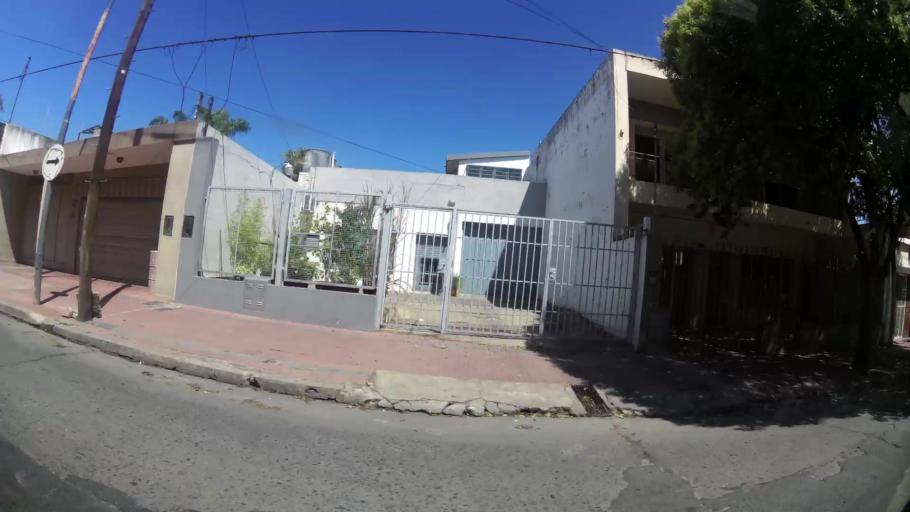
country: AR
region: Cordoba
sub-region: Departamento de Capital
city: Cordoba
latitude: -31.4186
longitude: -64.2081
